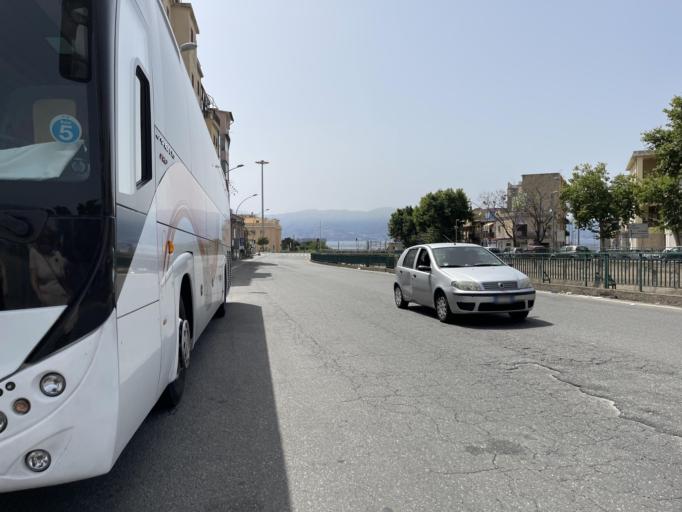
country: IT
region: Calabria
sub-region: Provincia di Reggio Calabria
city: Reggio Calabria
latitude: 38.1010
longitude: 15.6369
